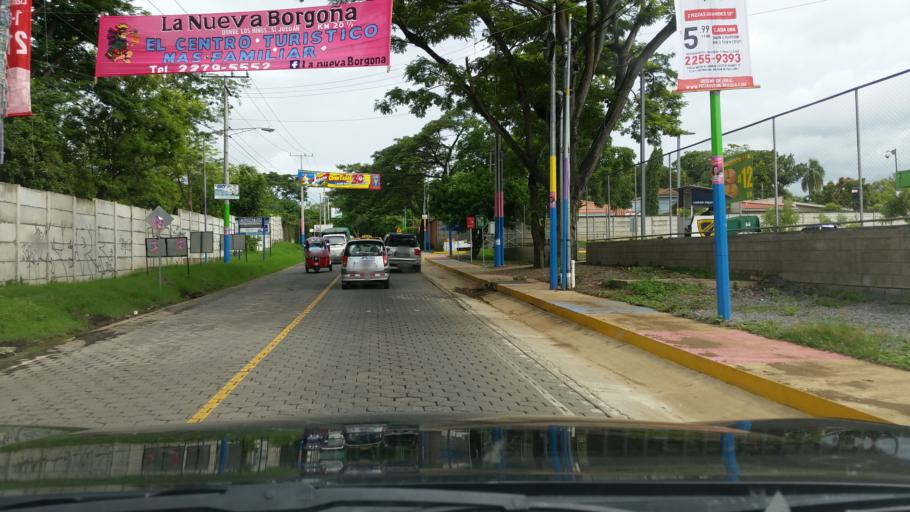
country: NI
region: Masaya
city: Ticuantepe
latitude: 12.0542
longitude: -86.2032
